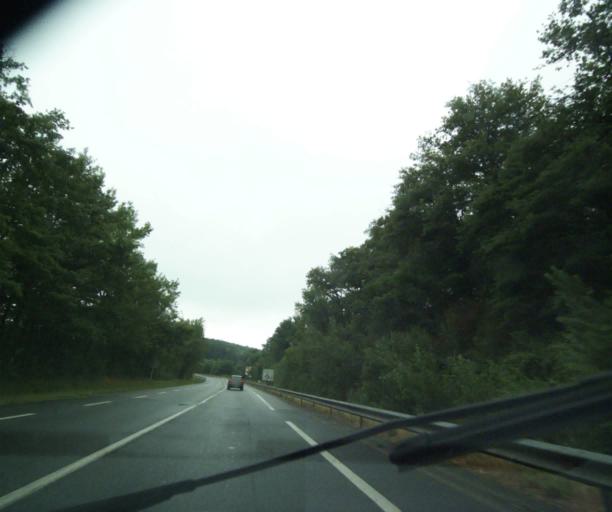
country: FR
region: Midi-Pyrenees
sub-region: Departement du Tarn
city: Le Garric
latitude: 43.9930
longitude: 2.1737
